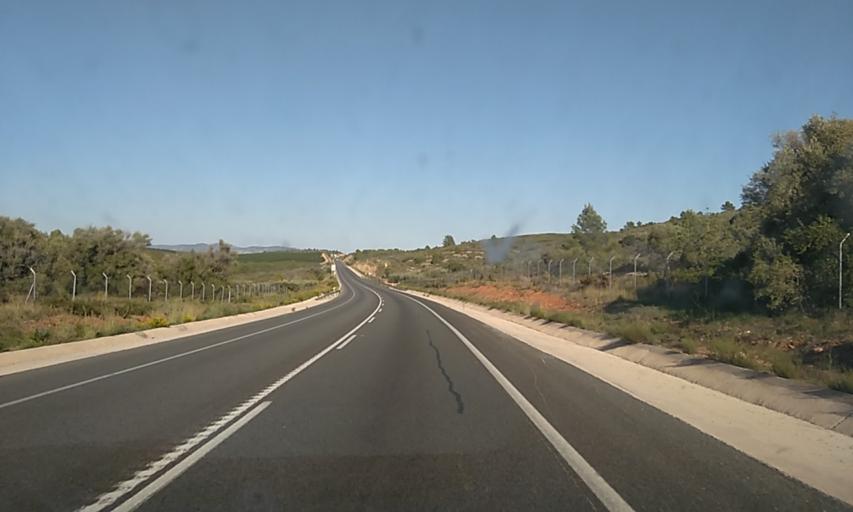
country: ES
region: Valencia
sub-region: Provincia de Castello
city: Torreblanca
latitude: 40.2106
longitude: 0.1416
